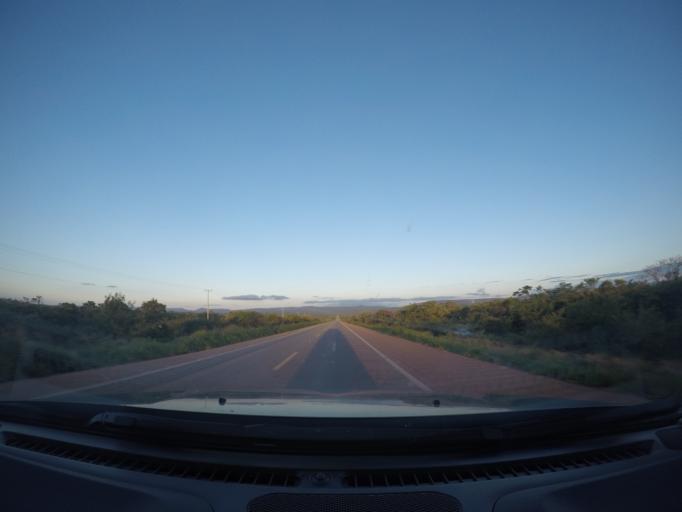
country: BR
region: Bahia
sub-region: Seabra
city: Seabra
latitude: -12.4083
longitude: -41.9642
